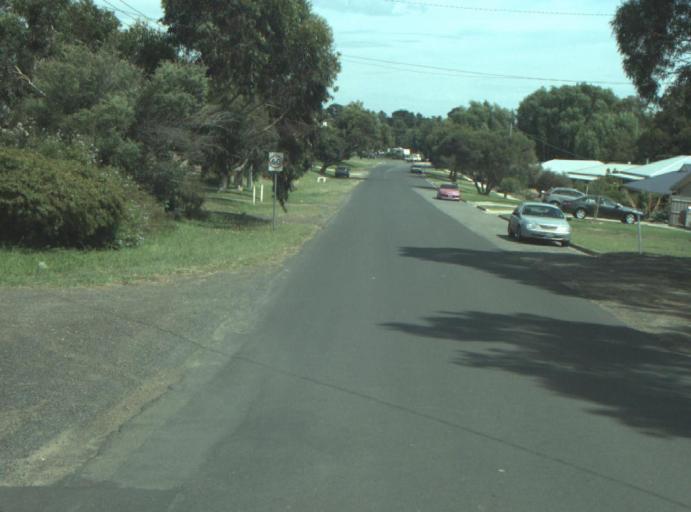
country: AU
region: Victoria
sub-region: Greater Geelong
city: Clifton Springs
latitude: -38.1800
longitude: 144.5660
